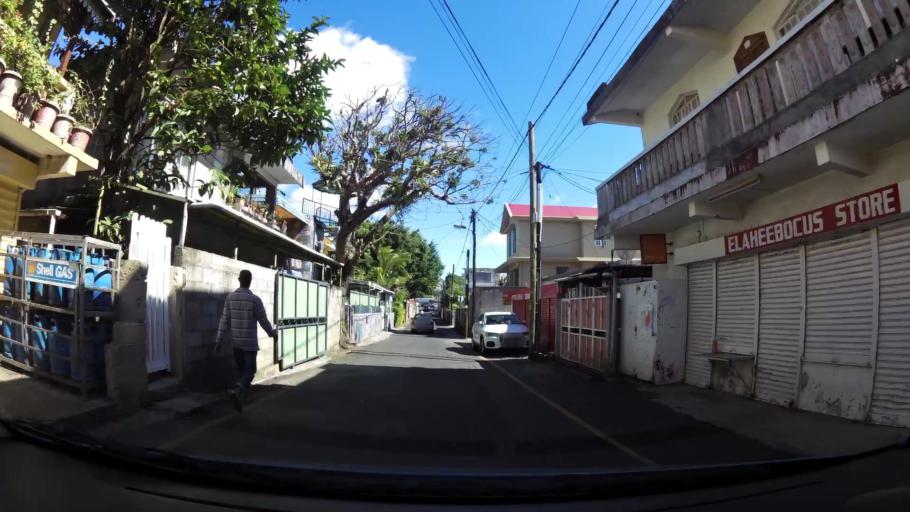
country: MU
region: Plaines Wilhems
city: Vacoas
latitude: -20.2959
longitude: 57.4848
